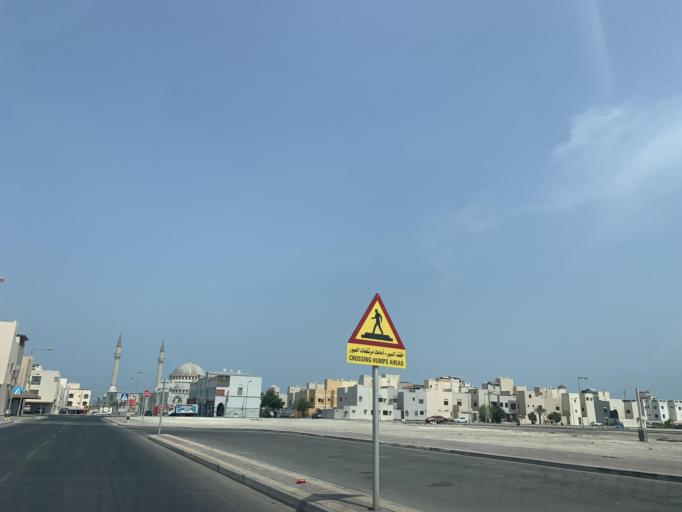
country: BH
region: Muharraq
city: Al Hadd
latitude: 26.2713
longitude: 50.6579
